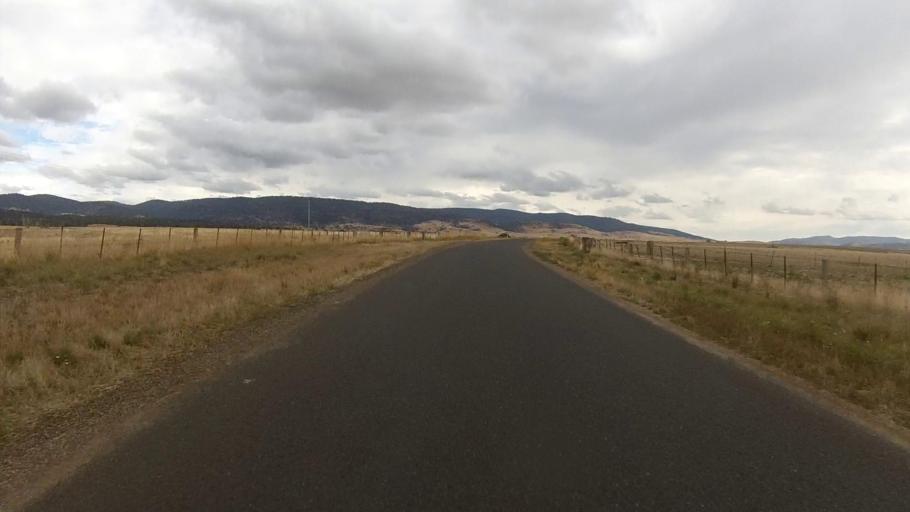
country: AU
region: Tasmania
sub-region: Northern Midlands
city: Evandale
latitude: -41.8260
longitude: 147.7929
